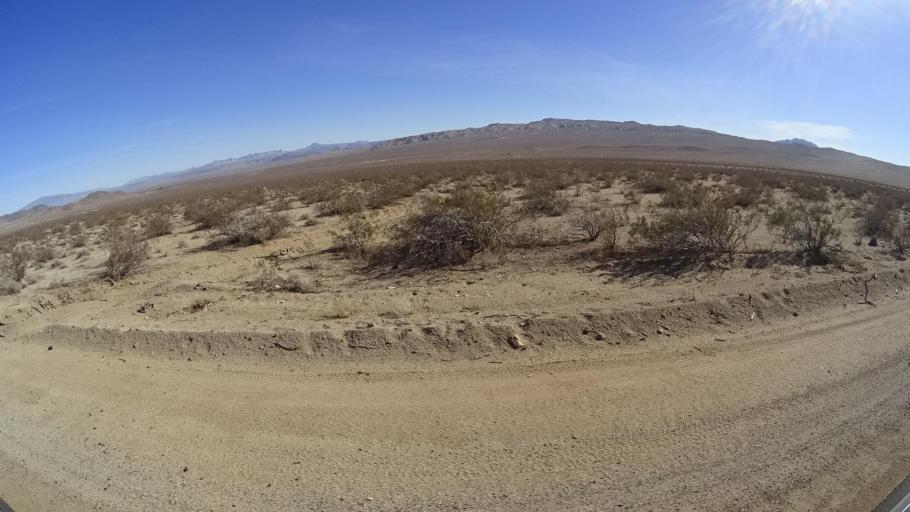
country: US
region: California
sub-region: Kern County
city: Ridgecrest
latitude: 35.5203
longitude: -117.6033
